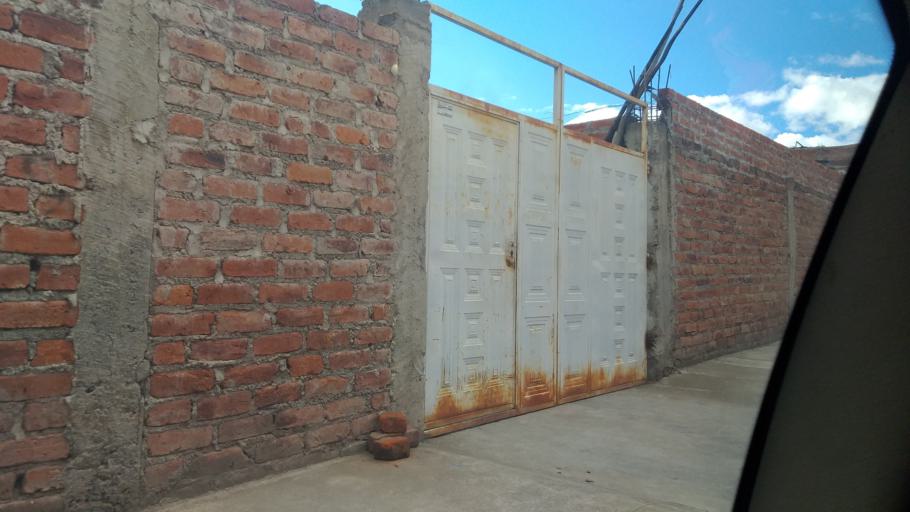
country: EC
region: Chimborazo
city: Riobamba
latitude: -1.6895
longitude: -78.6289
